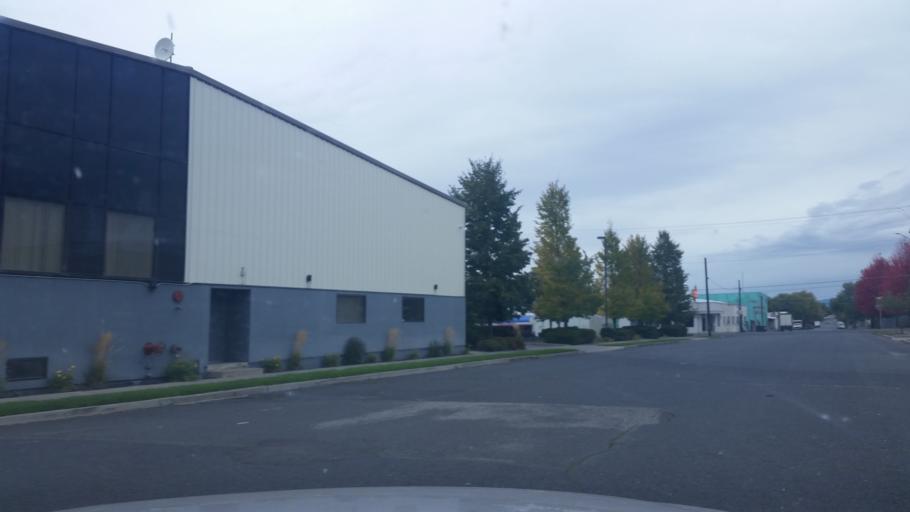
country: US
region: Washington
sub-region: Spokane County
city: Spokane
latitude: 47.6581
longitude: -117.3887
